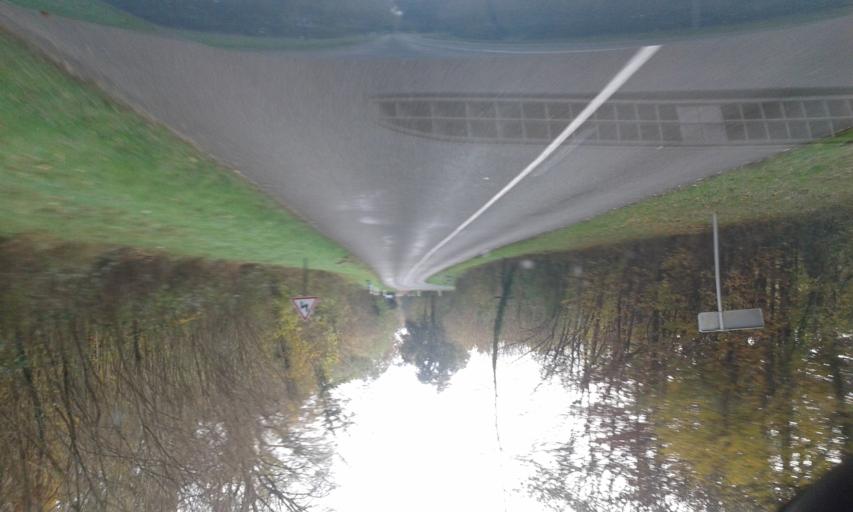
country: FR
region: Centre
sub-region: Departement du Loiret
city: Jouy-le-Potier
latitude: 47.7909
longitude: 1.8683
